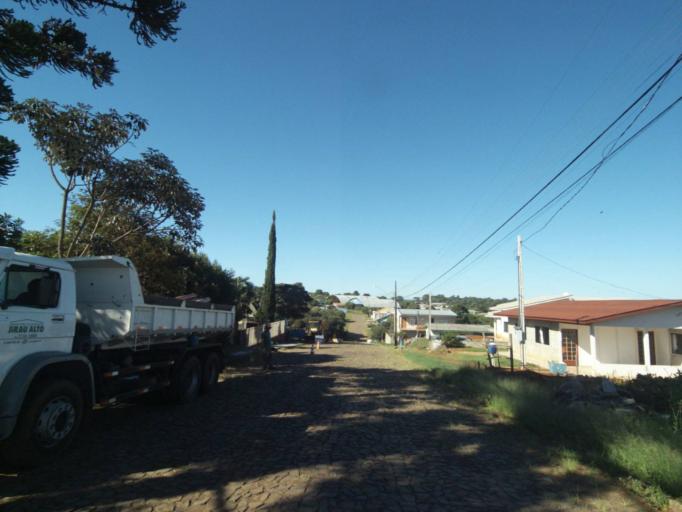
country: BR
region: Parana
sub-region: Pinhao
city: Pinhao
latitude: -25.8393
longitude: -52.0288
